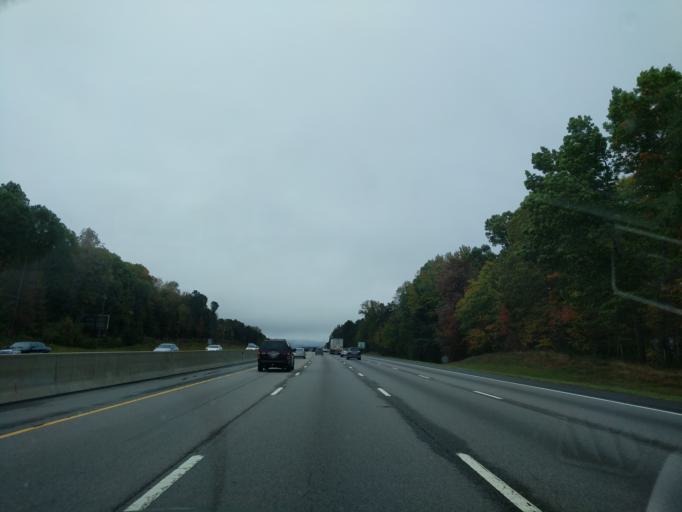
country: US
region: North Carolina
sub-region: Orange County
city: Hillsborough
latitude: 36.0741
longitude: -79.1832
